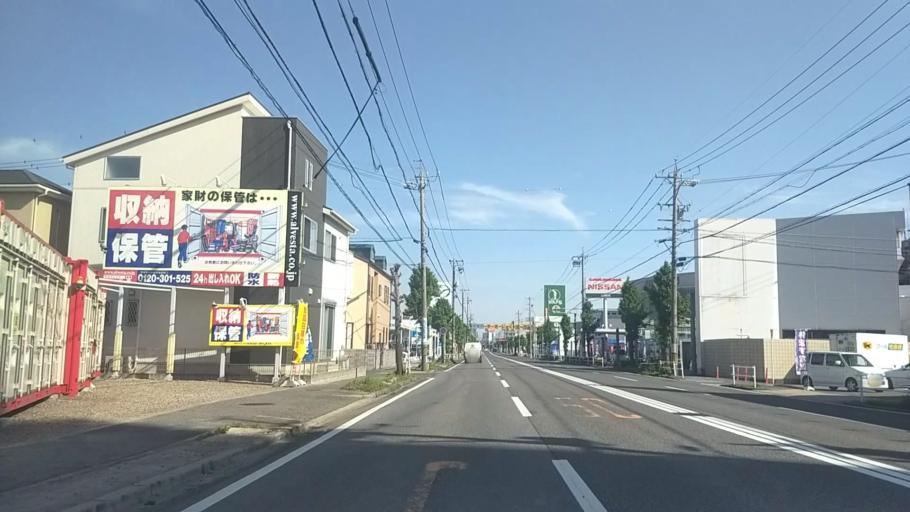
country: JP
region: Aichi
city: Anjo
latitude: 34.9617
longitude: 137.0701
